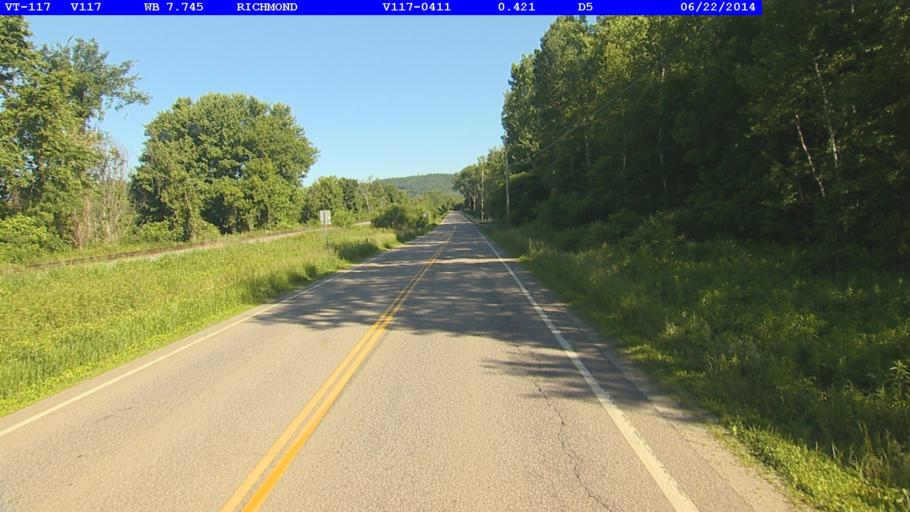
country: US
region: Vermont
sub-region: Chittenden County
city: Williston
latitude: 44.4286
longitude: -73.0163
